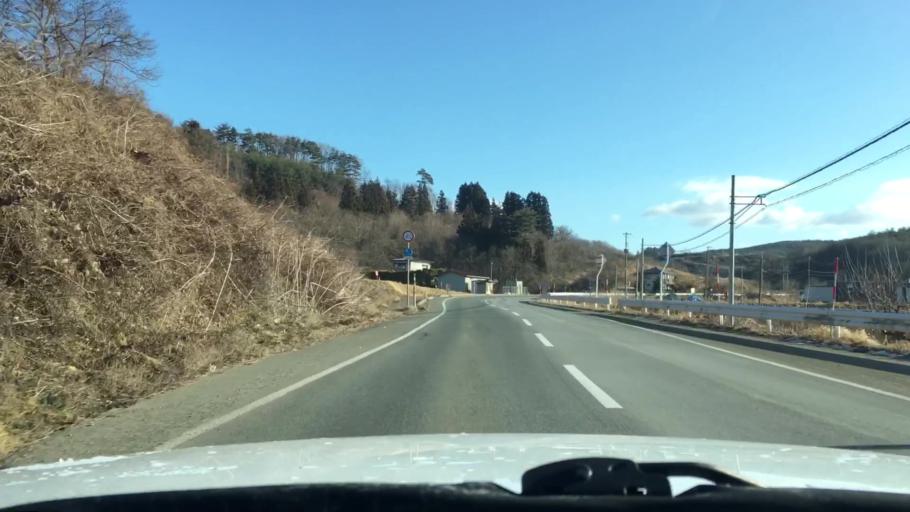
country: JP
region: Iwate
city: Morioka-shi
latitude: 39.6624
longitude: 141.1989
